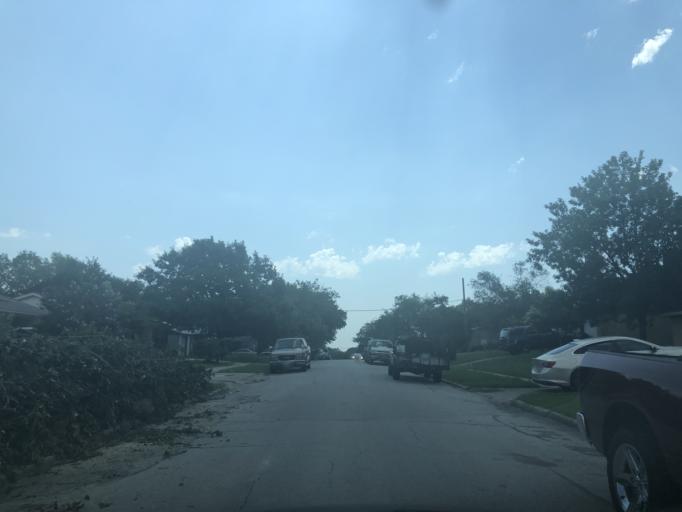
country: US
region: Texas
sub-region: Dallas County
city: Grand Prairie
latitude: 32.7242
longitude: -97.0099
